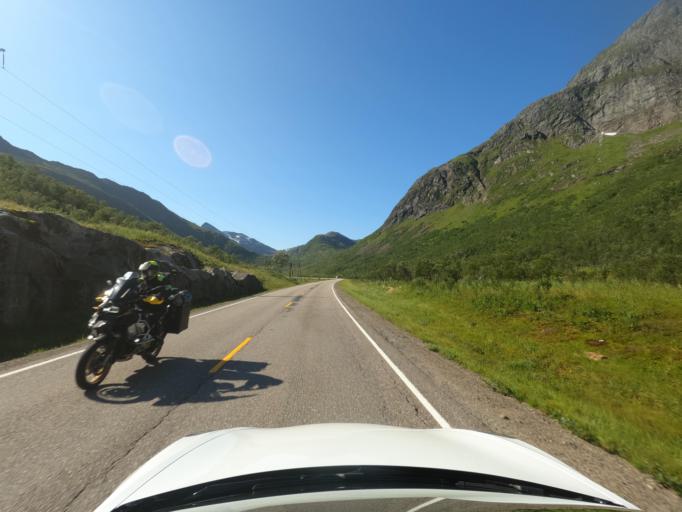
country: NO
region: Nordland
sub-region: Lodingen
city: Lodingen
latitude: 68.5007
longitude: 15.7067
